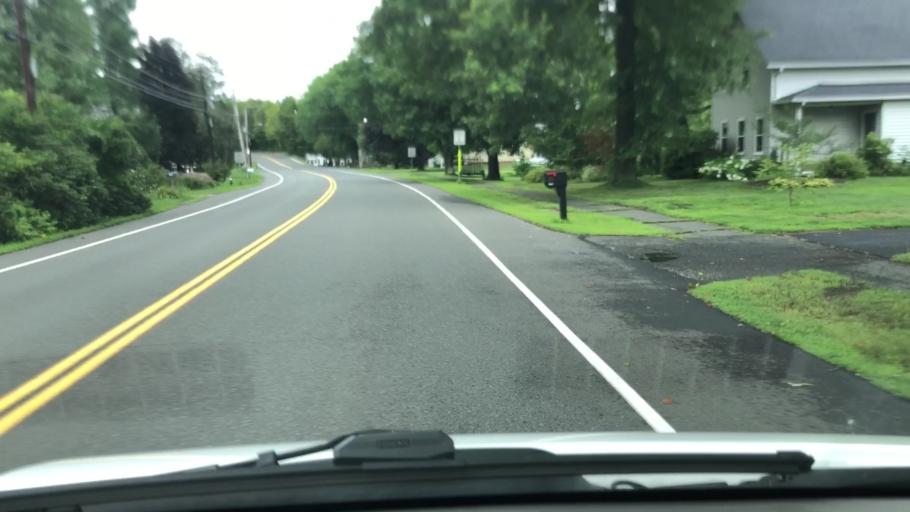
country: US
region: Massachusetts
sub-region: Franklin County
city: South Deerfield
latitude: 42.4931
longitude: -72.6065
